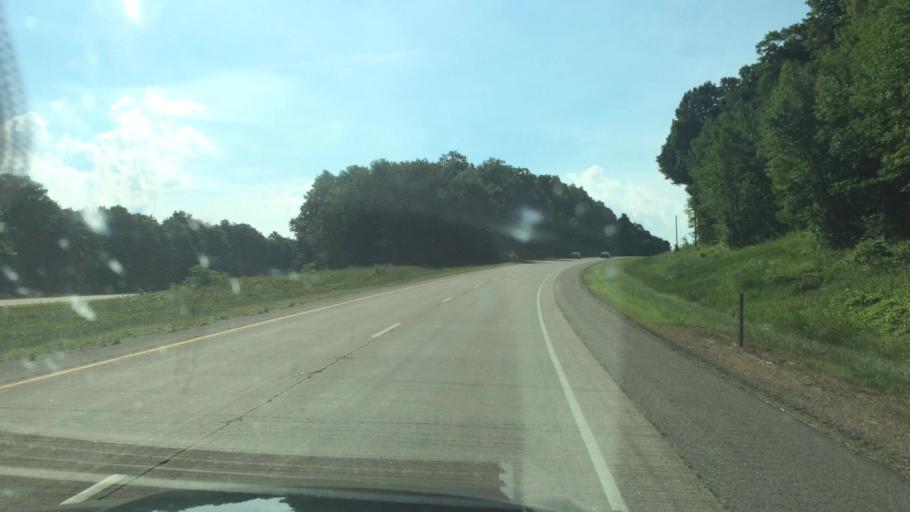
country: US
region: Wisconsin
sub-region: Shawano County
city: Wittenberg
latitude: 44.8237
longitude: -89.0607
